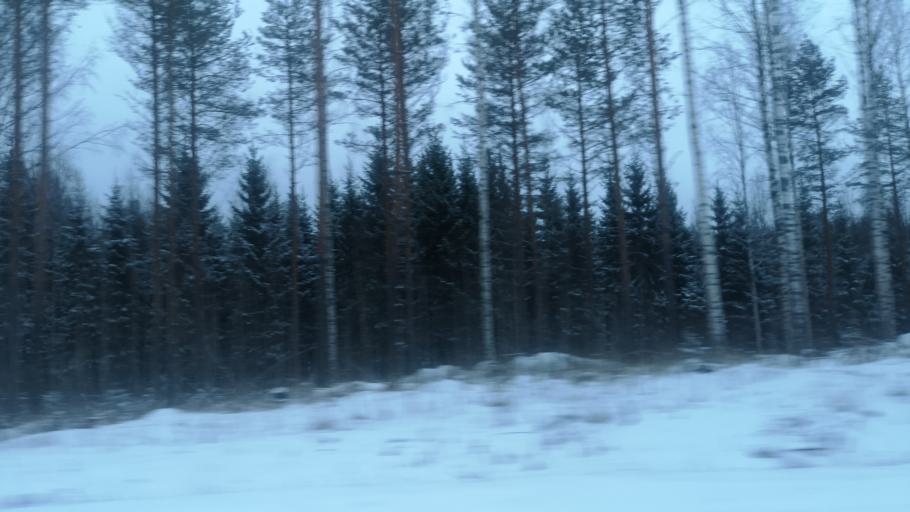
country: FI
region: Southern Savonia
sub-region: Savonlinna
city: Enonkoski
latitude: 62.0938
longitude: 28.6701
